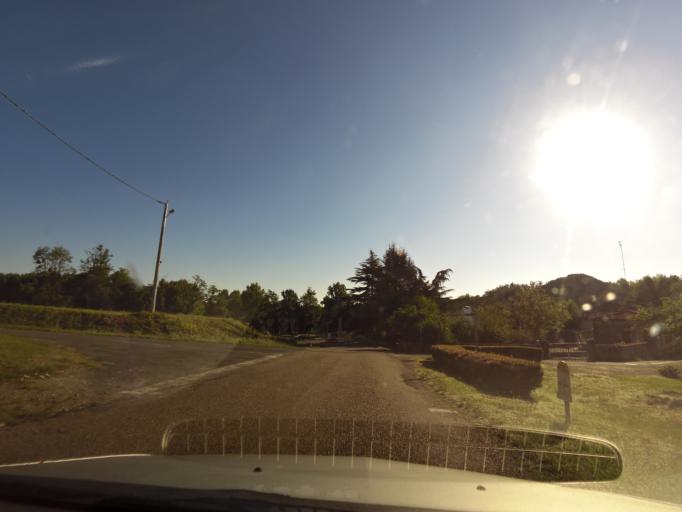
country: FR
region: Aquitaine
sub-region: Departement de la Gironde
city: Gironde-sur-Dropt
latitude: 44.5352
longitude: -0.0892
